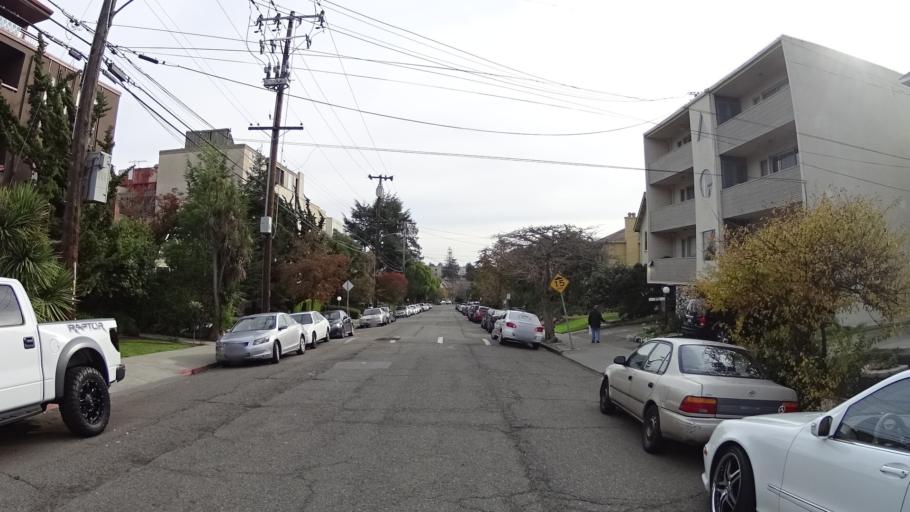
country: US
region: California
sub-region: Alameda County
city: Oakland
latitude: 37.8124
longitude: -122.2522
